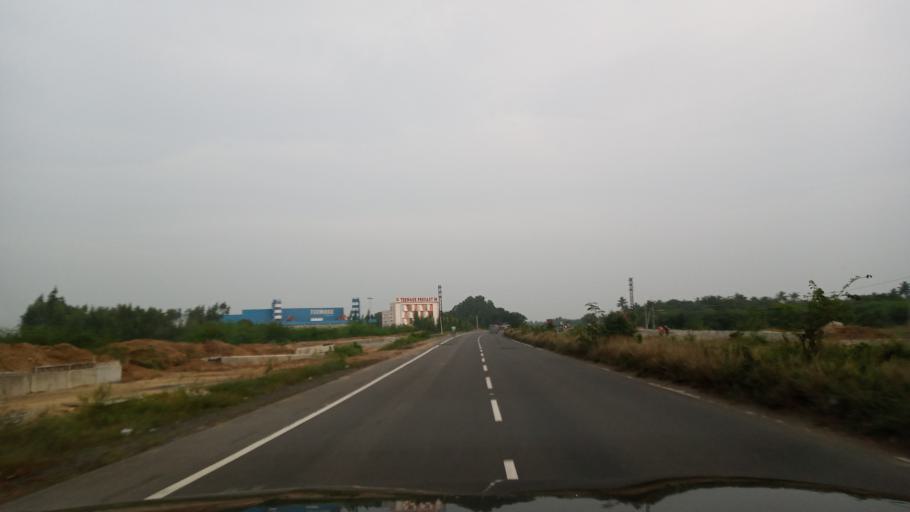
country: IN
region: Tamil Nadu
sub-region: Kancheepuram
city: Kanchipuram
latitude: 12.8826
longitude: 79.6003
